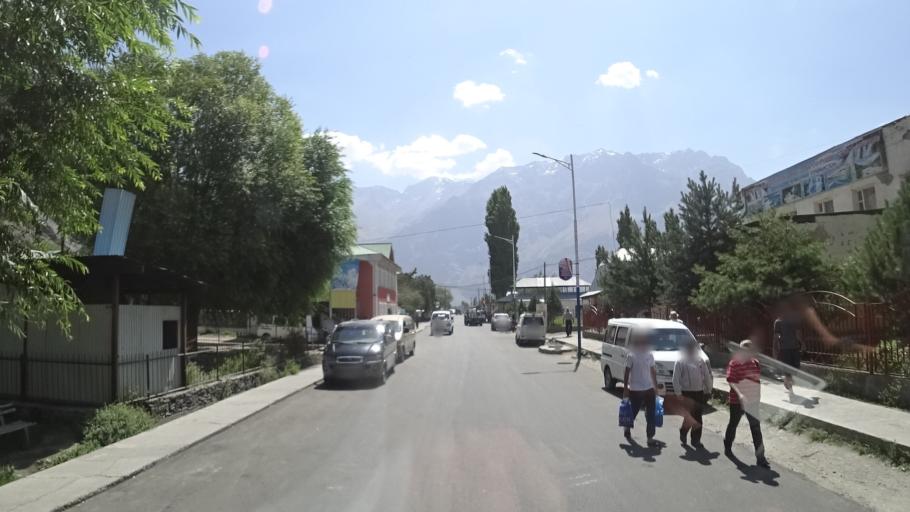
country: TJ
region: Gorno-Badakhshan
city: Rushon
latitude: 37.9473
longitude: 71.5573
